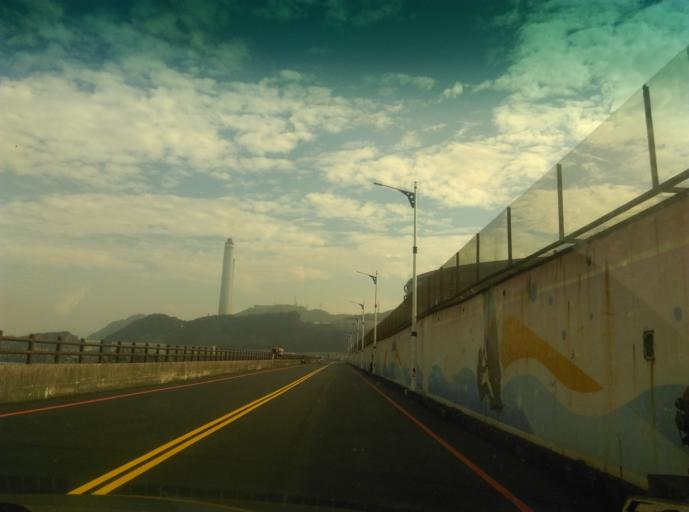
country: TW
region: Taiwan
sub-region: Keelung
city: Keelung
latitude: 25.1625
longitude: 121.7305
